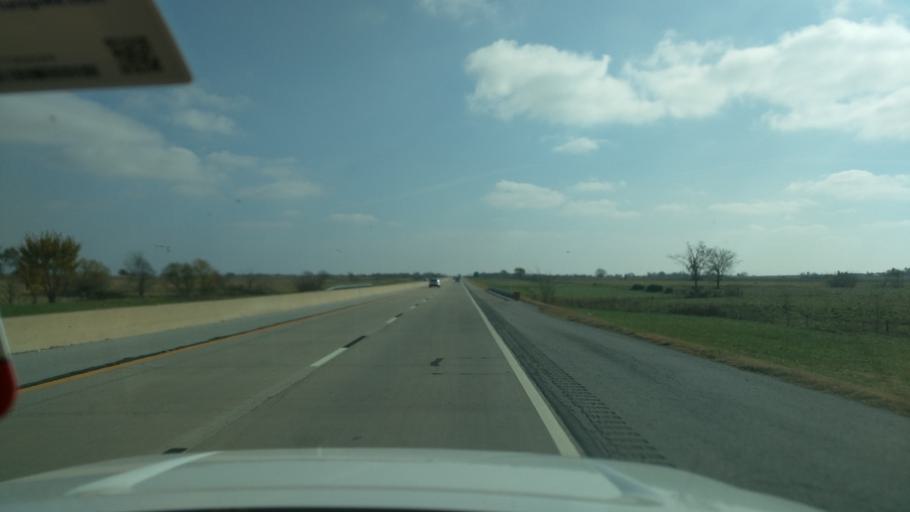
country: US
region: Oklahoma
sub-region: Wagoner County
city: Coweta
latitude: 35.9117
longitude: -95.5456
